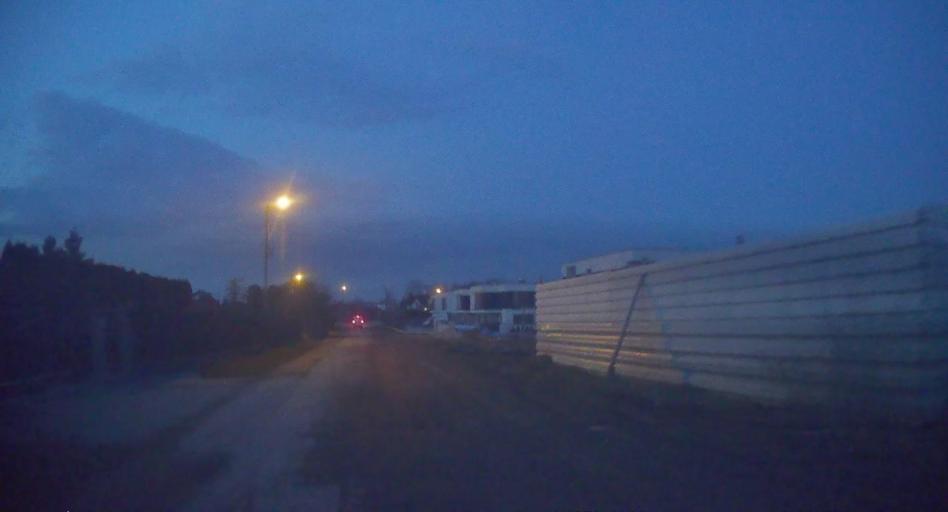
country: PL
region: Subcarpathian Voivodeship
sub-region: Powiat debicki
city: Debica
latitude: 50.0288
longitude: 21.3916
